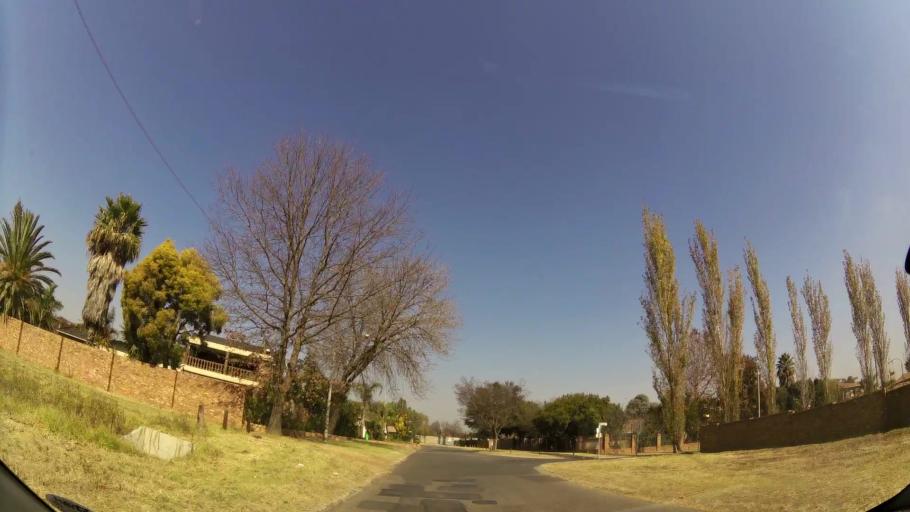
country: ZA
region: Gauteng
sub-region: Ekurhuleni Metropolitan Municipality
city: Boksburg
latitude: -26.1712
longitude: 28.2653
